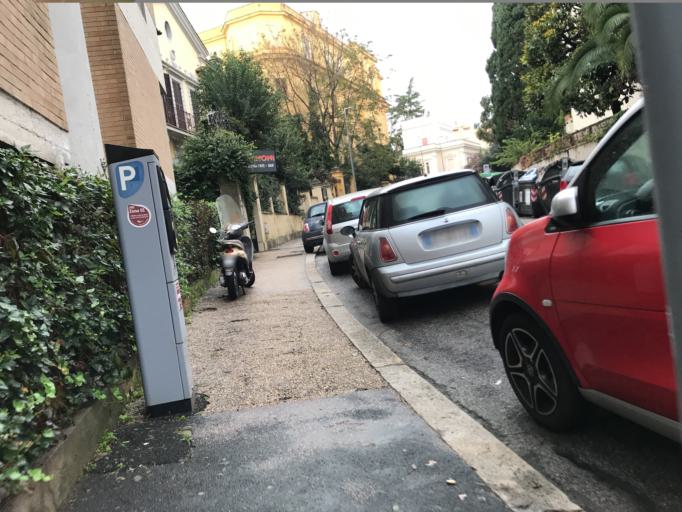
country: IT
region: Latium
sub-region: Citta metropolitana di Roma Capitale
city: Rome
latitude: 41.9150
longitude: 12.5149
